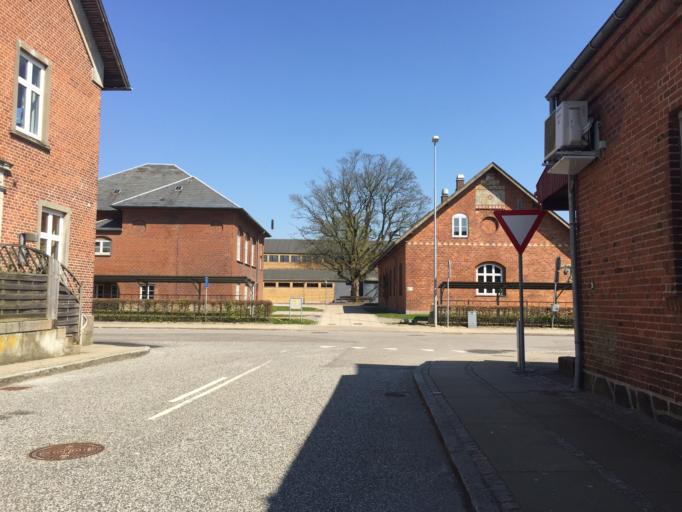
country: DK
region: South Denmark
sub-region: Vejle Kommune
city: Jelling
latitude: 55.7548
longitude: 9.4196
